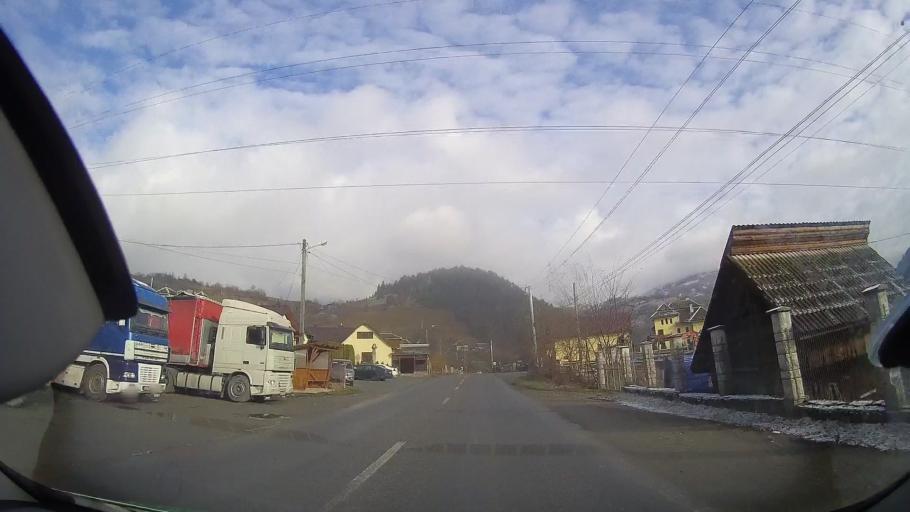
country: RO
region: Alba
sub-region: Comuna Bistra
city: Bistra
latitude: 46.3779
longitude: 23.1180
